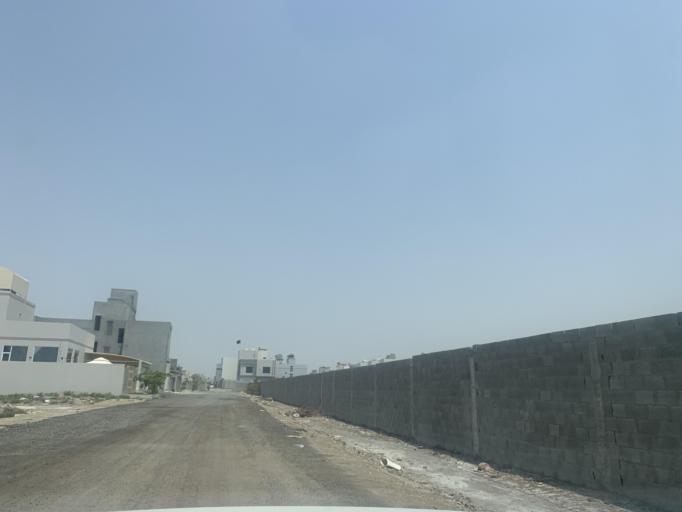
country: BH
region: Central Governorate
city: Madinat Hamad
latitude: 26.1296
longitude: 50.4655
